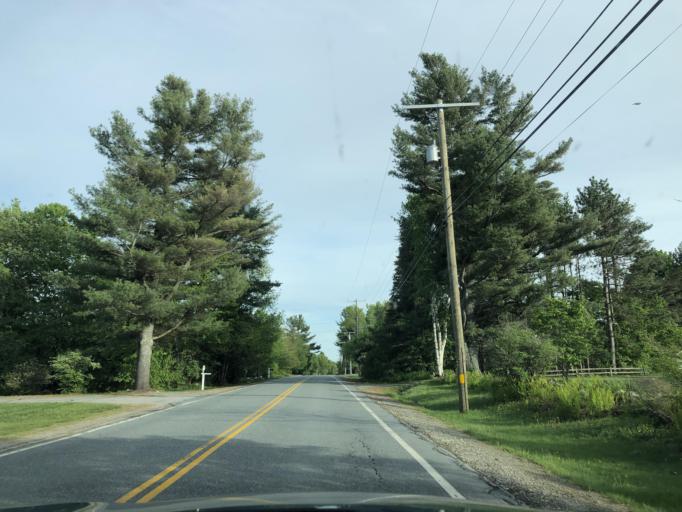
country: US
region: New Hampshire
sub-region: Merrimack County
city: New London
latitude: 43.4263
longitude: -71.9956
